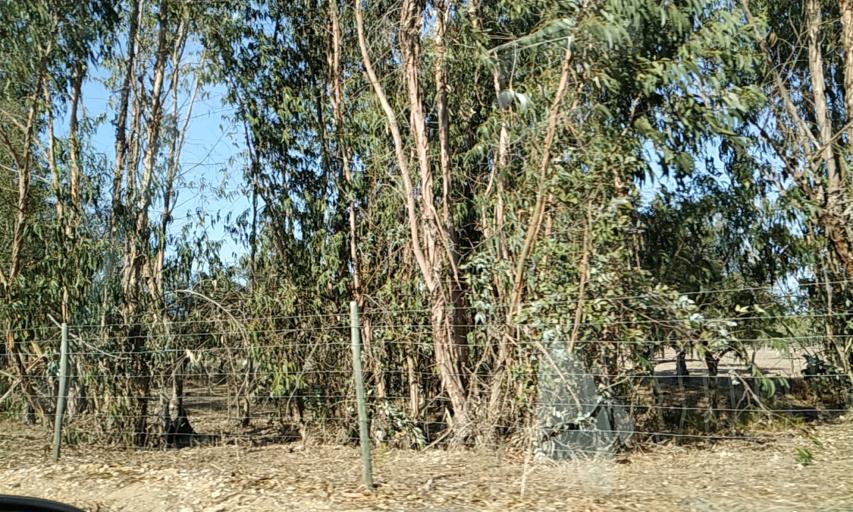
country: PT
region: Santarem
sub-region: Almeirim
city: Fazendas de Almeirim
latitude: 39.1359
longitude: -8.6101
